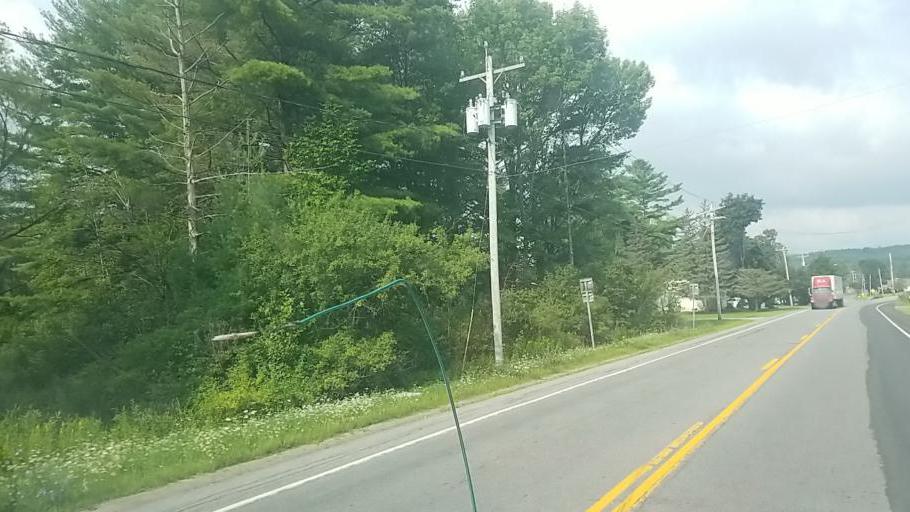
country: US
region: New York
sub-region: Fulton County
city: Gloversville
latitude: 43.0545
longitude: -74.3774
